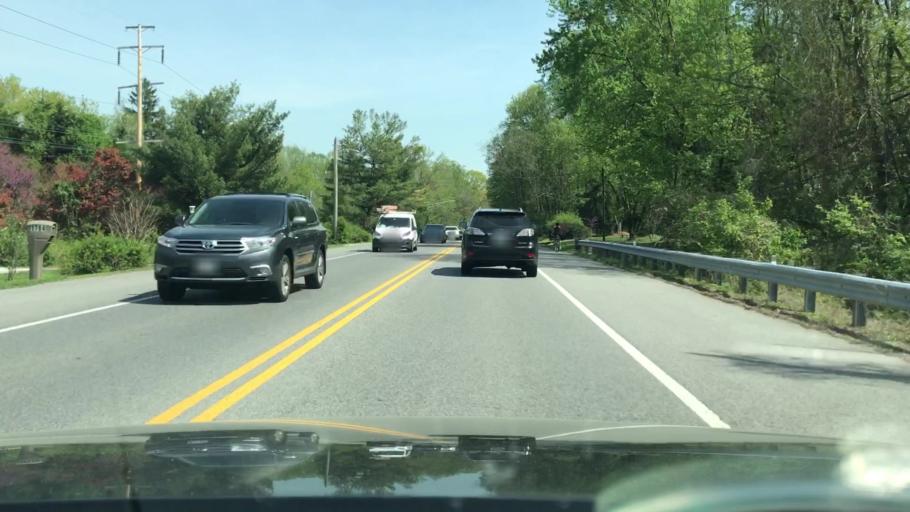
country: US
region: Maryland
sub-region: Anne Arundel County
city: Crownsville
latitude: 39.0097
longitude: -76.5644
